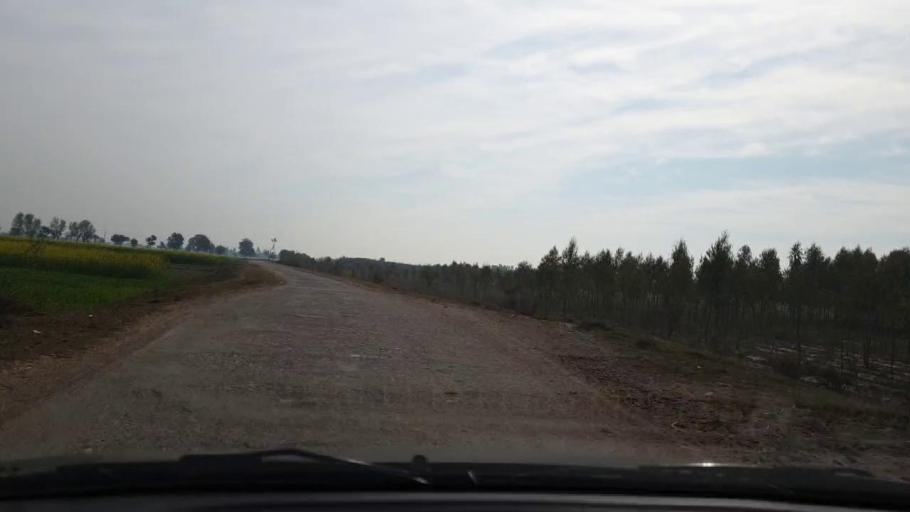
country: PK
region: Sindh
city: Shahpur Chakar
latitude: 26.1807
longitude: 68.6716
